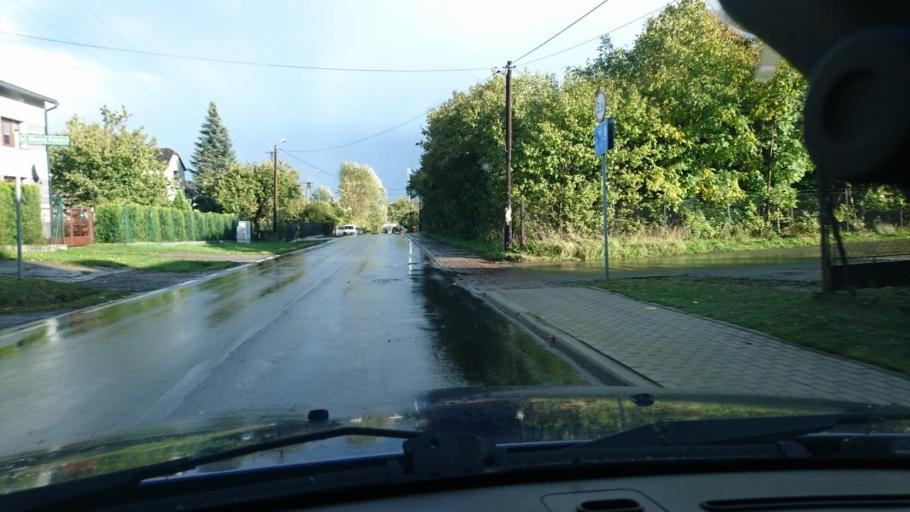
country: PL
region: Silesian Voivodeship
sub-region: Bielsko-Biala
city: Bielsko-Biala
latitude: 49.8577
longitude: 19.0216
